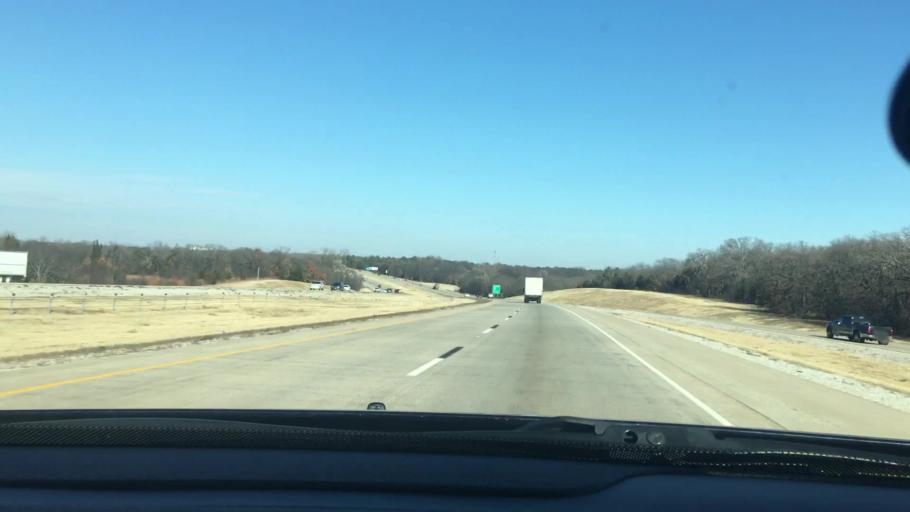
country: US
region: Oklahoma
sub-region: Carter County
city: Ardmore
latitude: 34.1409
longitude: -97.1554
